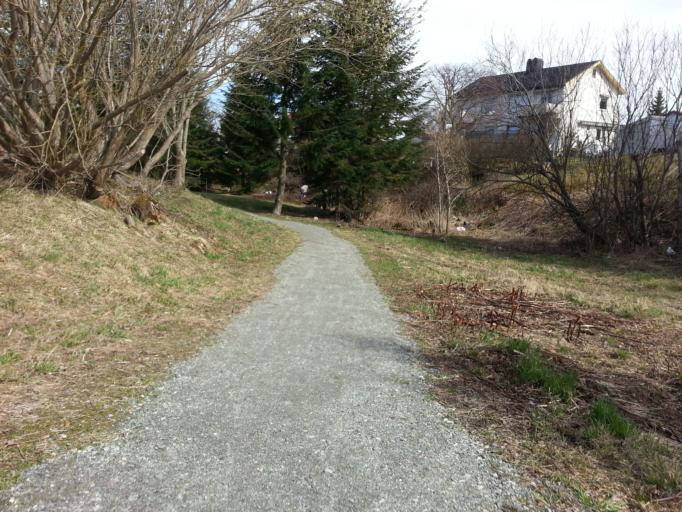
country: NO
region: Sor-Trondelag
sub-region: Trondheim
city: Trondheim
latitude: 63.4188
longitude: 10.4422
